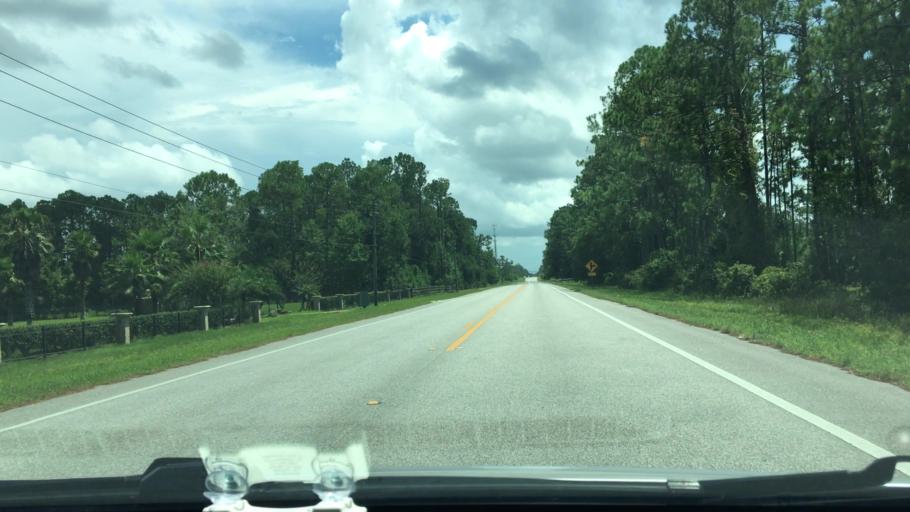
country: US
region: Florida
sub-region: Volusia County
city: Samsula-Spruce Creek
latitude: 29.0207
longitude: -81.0674
